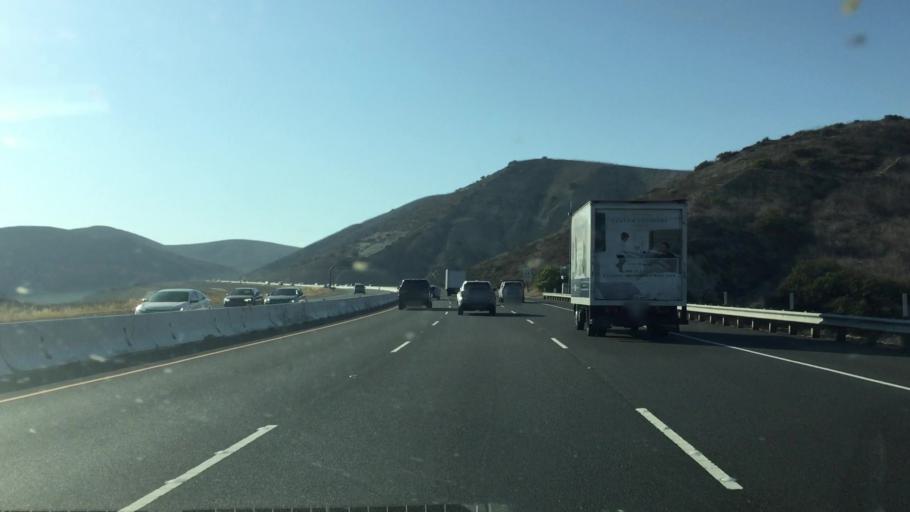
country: US
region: California
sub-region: Orange County
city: North Tustin
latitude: 33.7453
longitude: -117.7204
